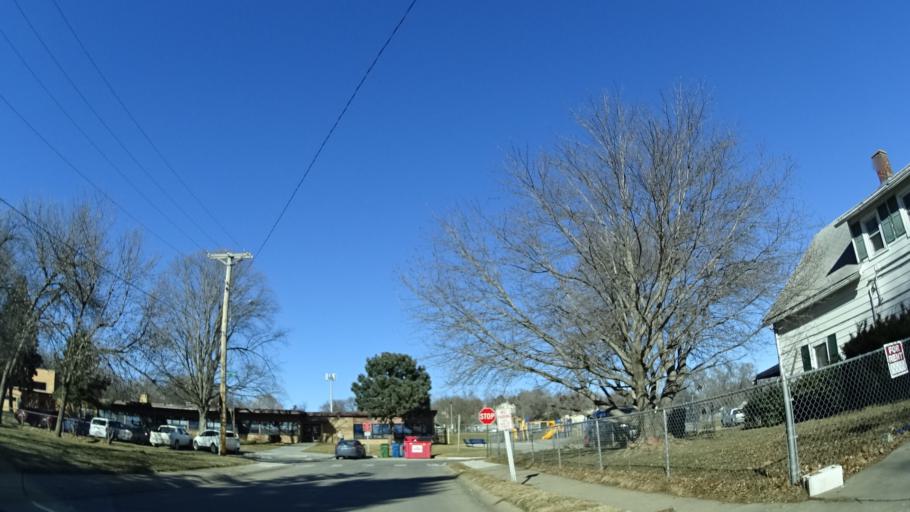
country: US
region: Nebraska
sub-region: Sarpy County
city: Bellevue
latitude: 41.1373
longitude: -95.8989
